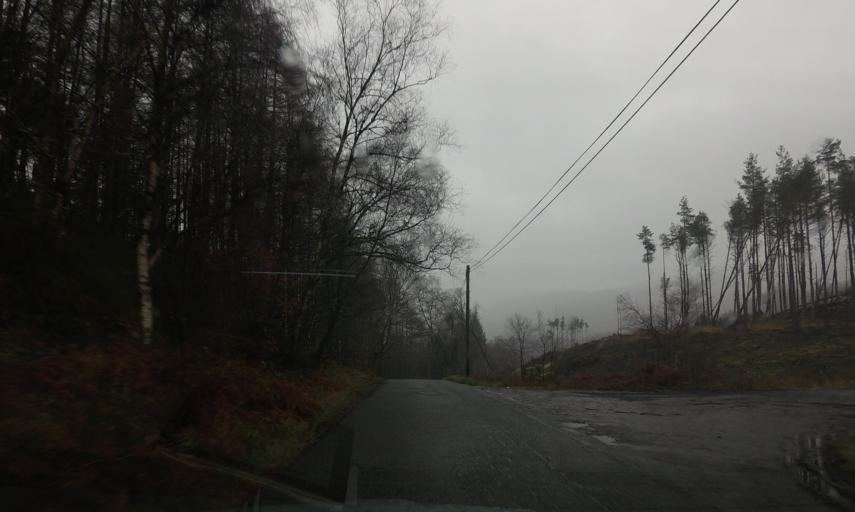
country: GB
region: Scotland
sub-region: West Dunbartonshire
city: Balloch
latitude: 56.1458
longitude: -4.6386
